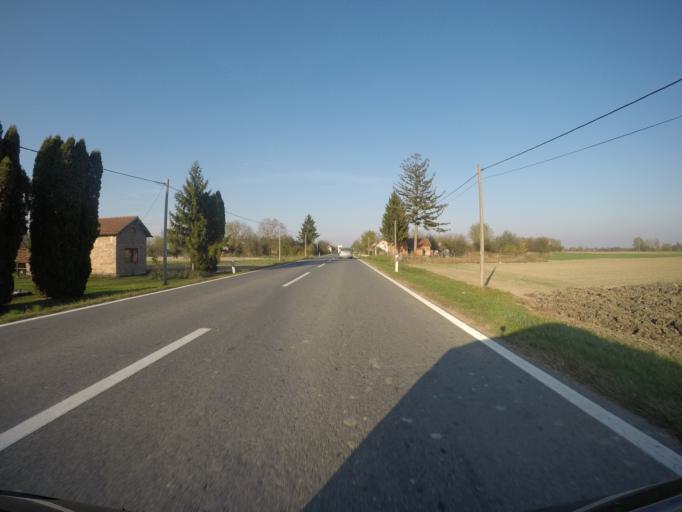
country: HU
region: Somogy
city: Barcs
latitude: 45.9290
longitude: 17.4576
